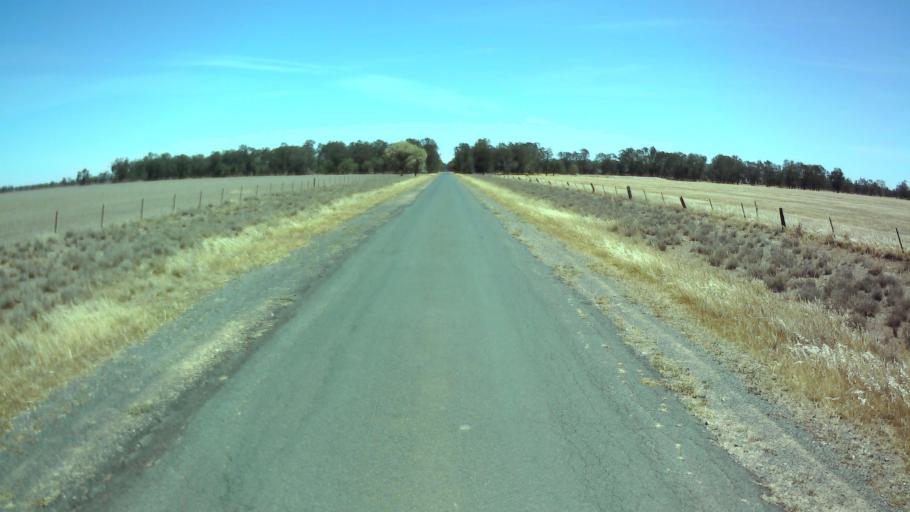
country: AU
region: New South Wales
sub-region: Weddin
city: Grenfell
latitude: -33.8644
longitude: 147.6931
